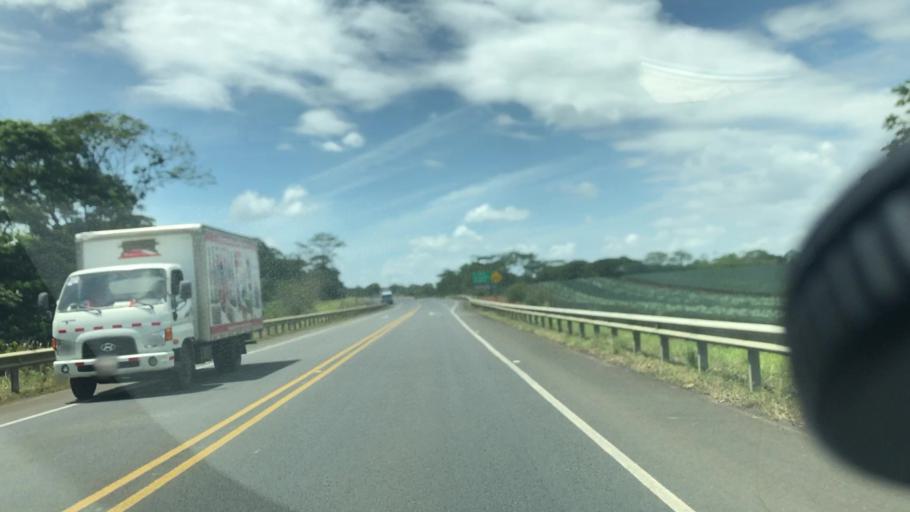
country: CR
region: Heredia
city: La Virgen
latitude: 10.4409
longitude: -84.1547
